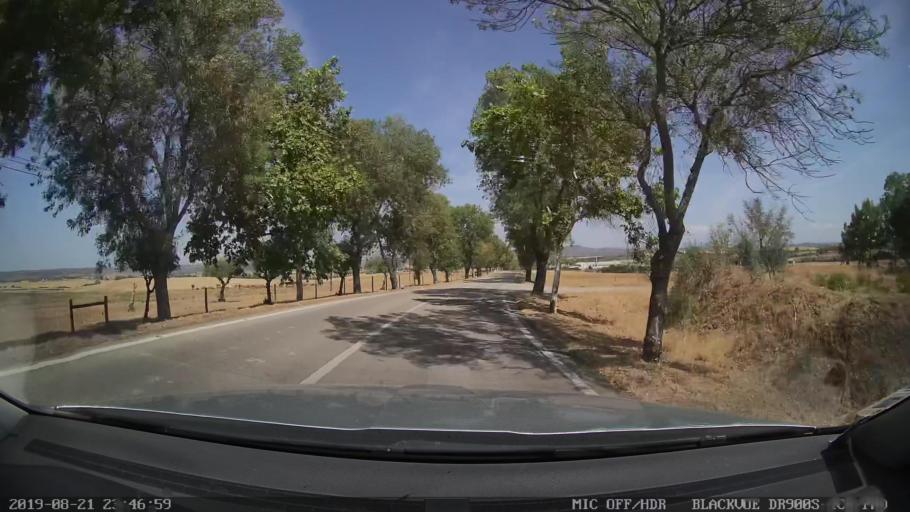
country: PT
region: Castelo Branco
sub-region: Idanha-A-Nova
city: Idanha-a-Nova
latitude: 39.8461
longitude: -7.2569
